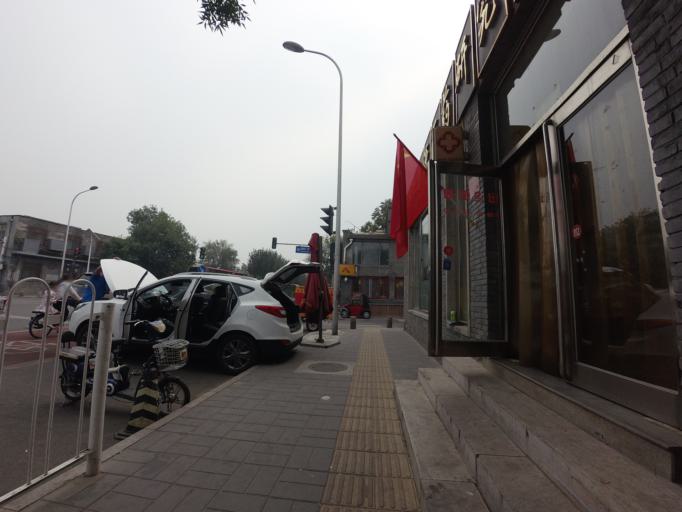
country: CN
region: Beijing
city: Jinrongjie
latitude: 39.9381
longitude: 116.3729
